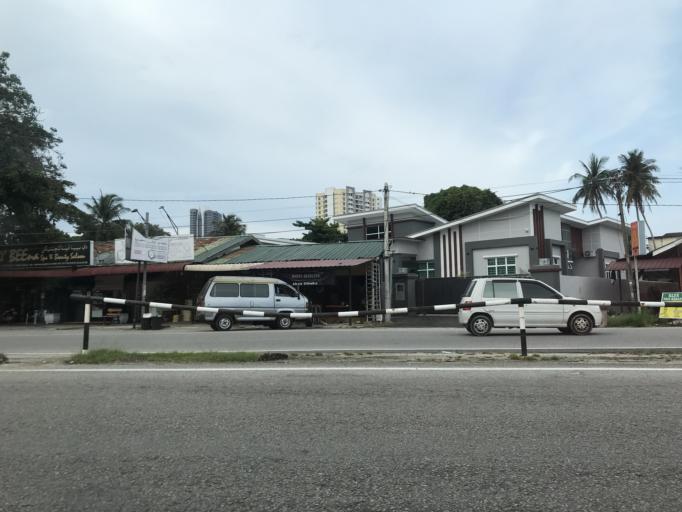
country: MY
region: Kelantan
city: Kota Bharu
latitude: 6.1153
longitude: 102.2368
